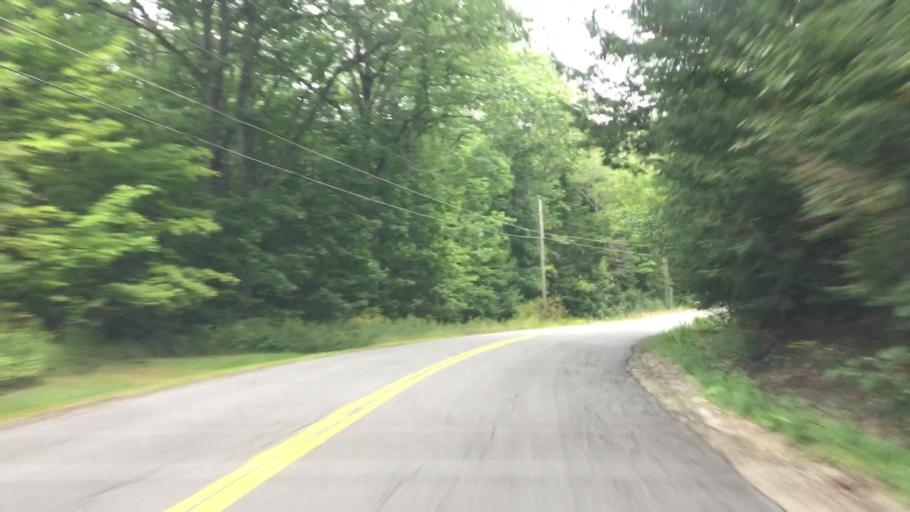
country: US
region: Maine
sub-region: Cumberland County
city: New Gloucester
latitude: 43.9057
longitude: -70.2146
